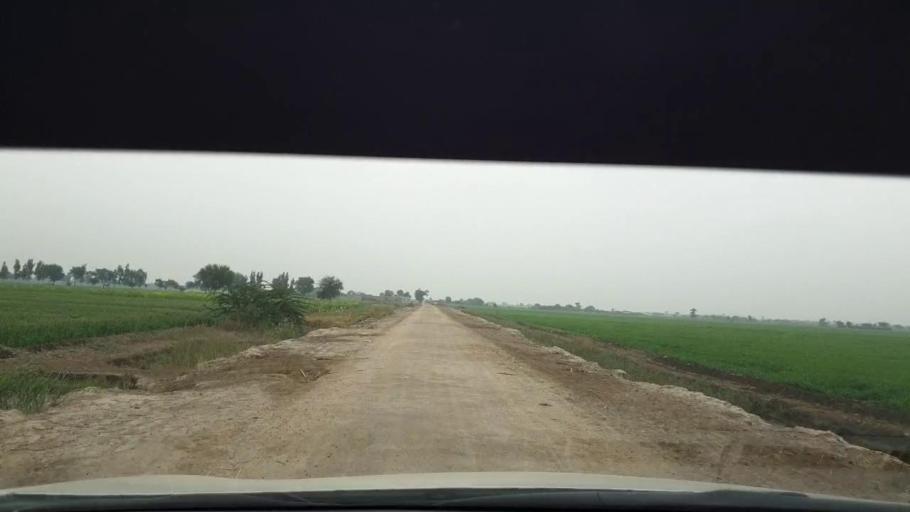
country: PK
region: Sindh
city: Berani
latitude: 25.7602
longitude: 68.8528
